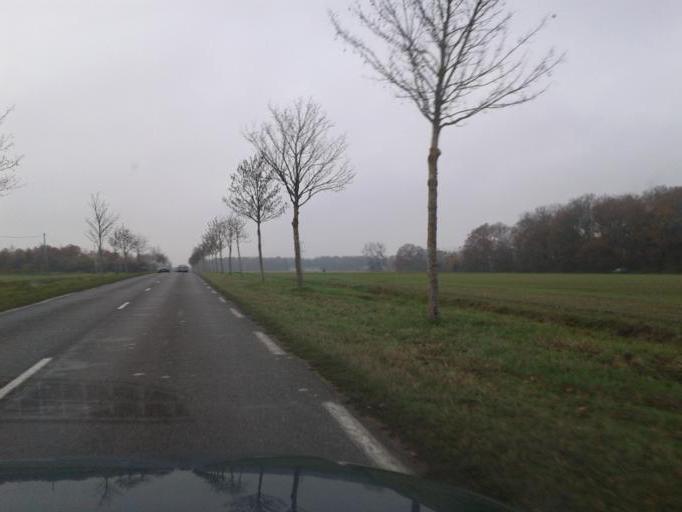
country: FR
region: Centre
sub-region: Departement du Loiret
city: Clery-Saint-Andre
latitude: 47.8082
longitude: 1.7402
